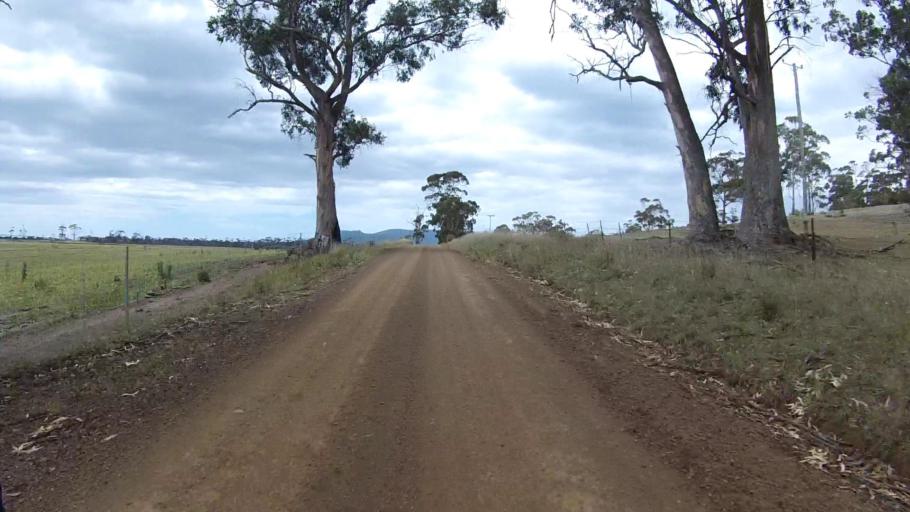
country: AU
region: Tasmania
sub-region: Sorell
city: Sorell
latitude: -42.6536
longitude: 147.9231
